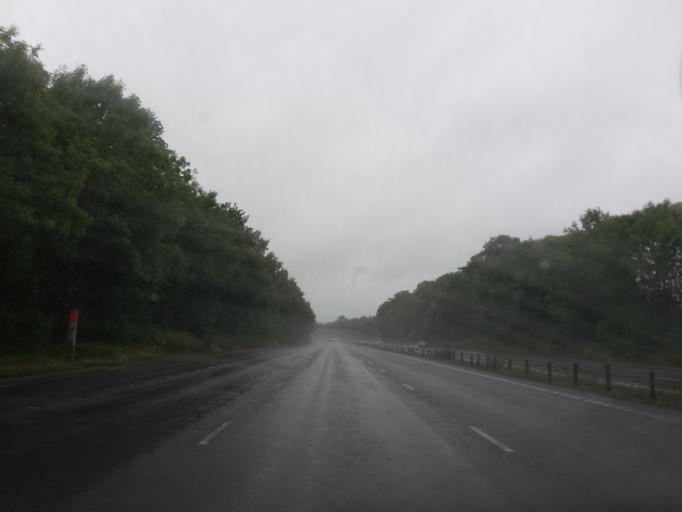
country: GB
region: England
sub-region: Warwickshire
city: Kenilworth
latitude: 52.3447
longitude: -1.5453
